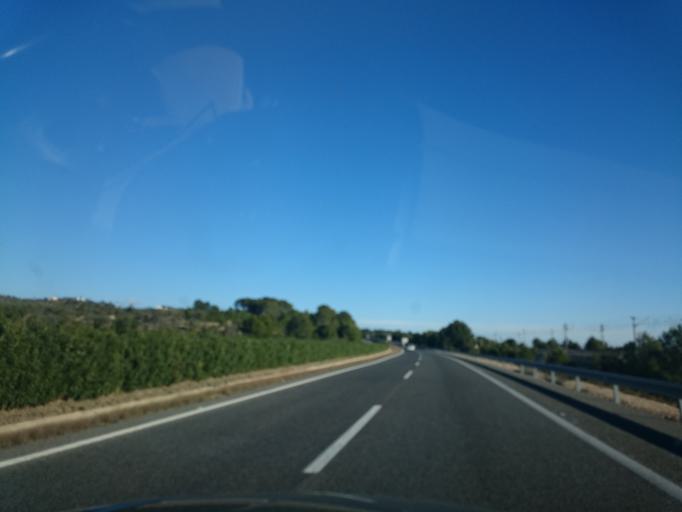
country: ES
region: Catalonia
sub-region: Provincia de Tarragona
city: L'Ampolla
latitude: 40.8322
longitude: 0.7390
